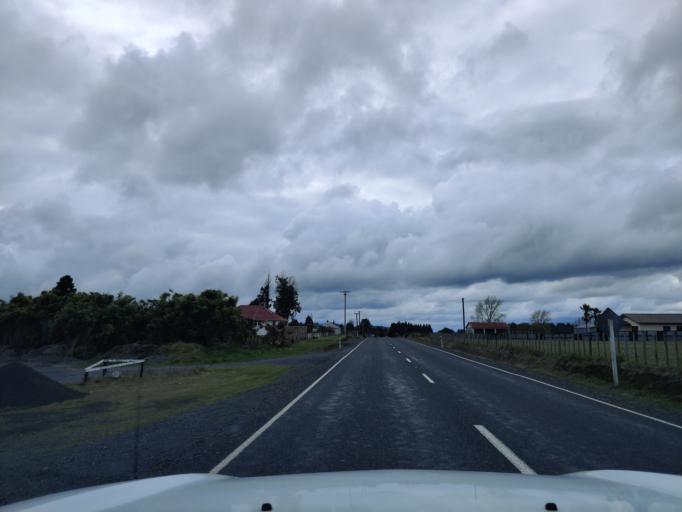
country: NZ
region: Waikato
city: Turangi
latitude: -39.0075
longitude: 175.3772
